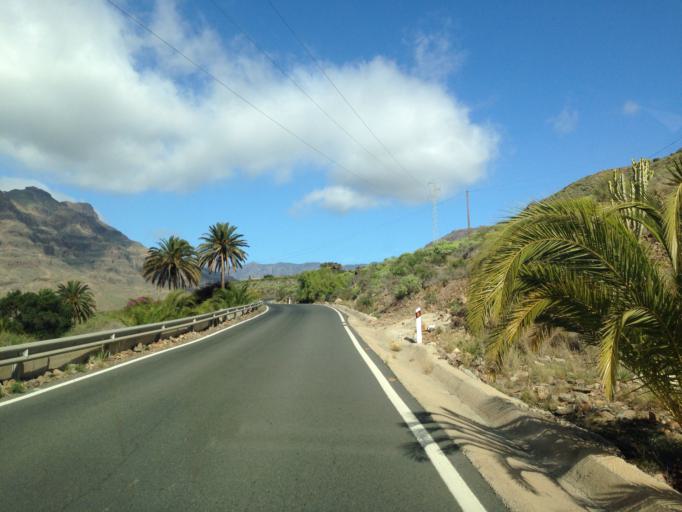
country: ES
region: Canary Islands
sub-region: Provincia de Las Palmas
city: Santa Lucia
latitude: 27.8557
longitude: -15.5660
